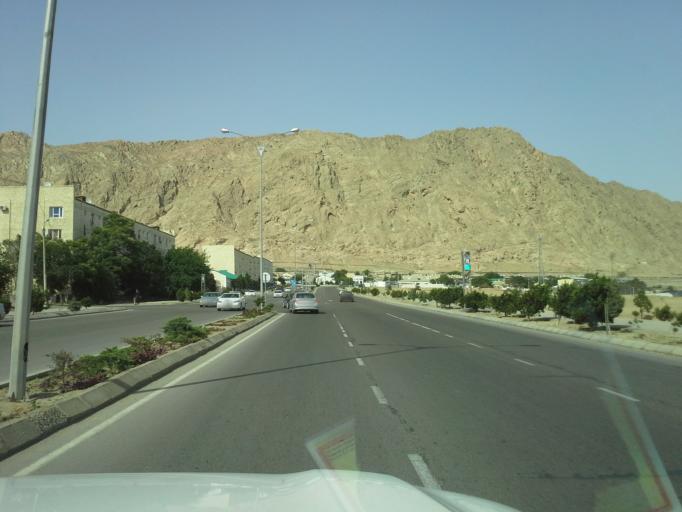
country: TM
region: Balkan
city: Turkmenbasy
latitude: 40.0066
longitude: 52.9978
